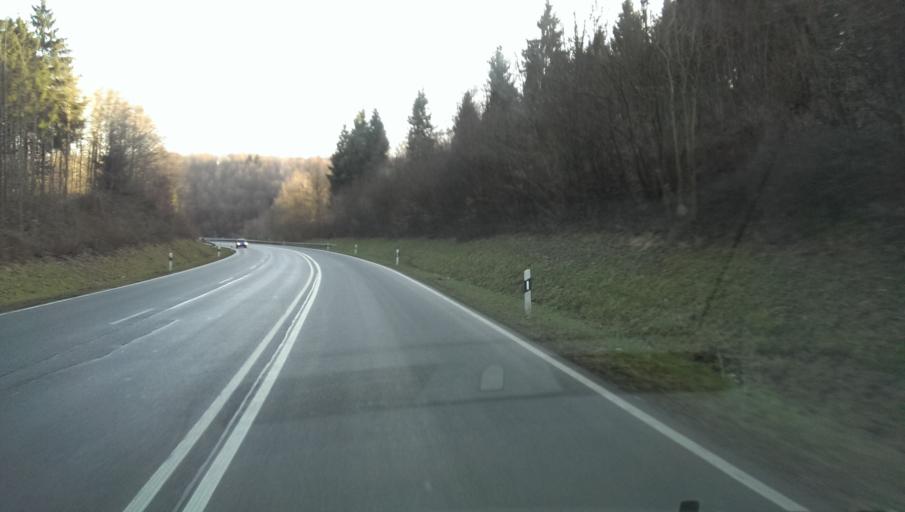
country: DE
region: North Rhine-Westphalia
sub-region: Regierungsbezirk Detmold
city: Bad Driburg
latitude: 51.7348
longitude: 8.9947
